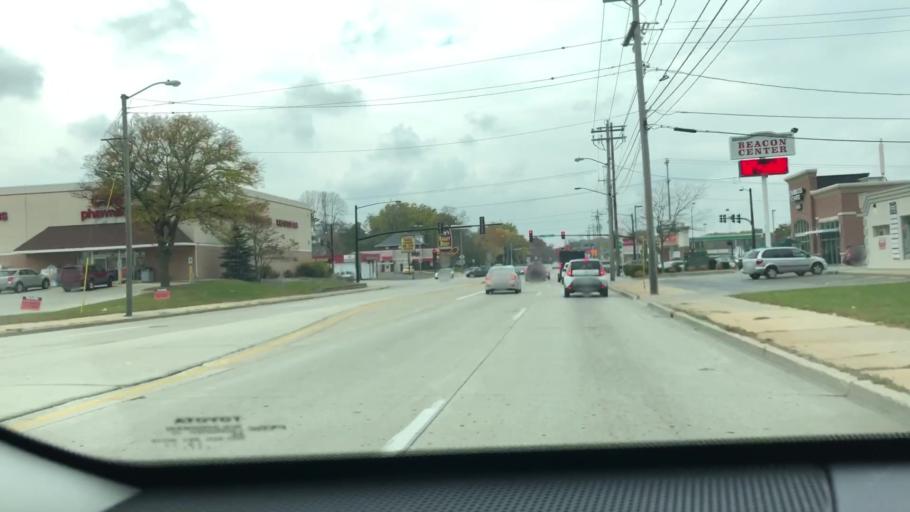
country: US
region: Wisconsin
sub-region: Brown County
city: Howard
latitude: 44.5233
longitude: -88.0627
